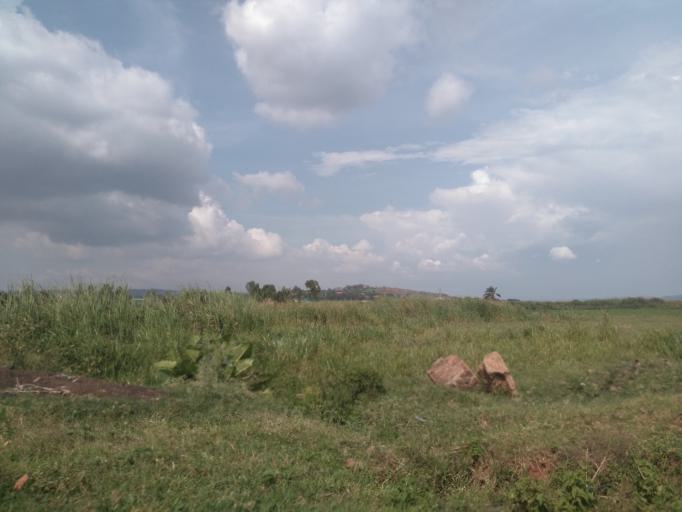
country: UG
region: Eastern Region
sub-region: Jinja District
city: Jinja
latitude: 0.4237
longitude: 33.2220
